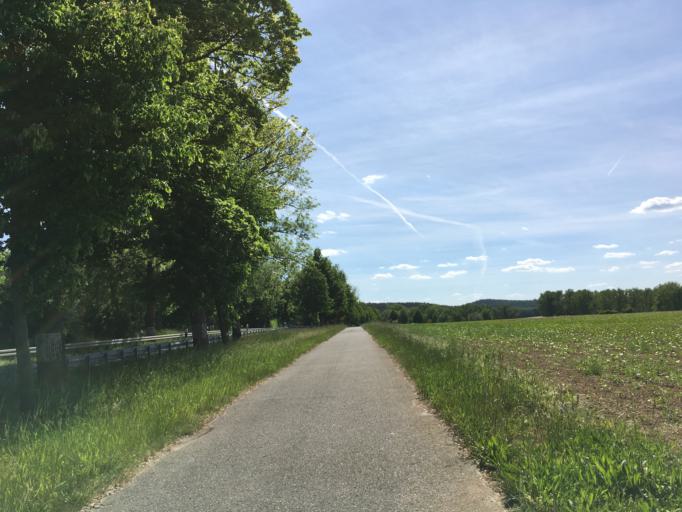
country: DE
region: Brandenburg
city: Oderberg
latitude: 52.8285
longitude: 14.0720
